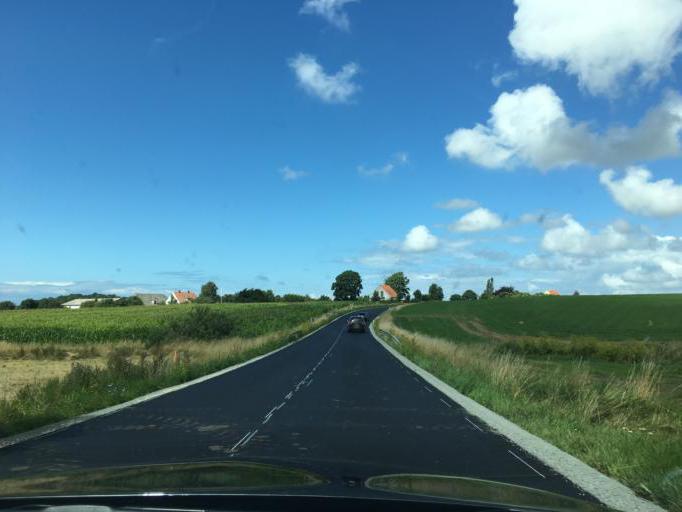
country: DK
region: Capital Region
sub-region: Gribskov Kommune
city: Helsinge
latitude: 56.0505
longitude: 12.1991
